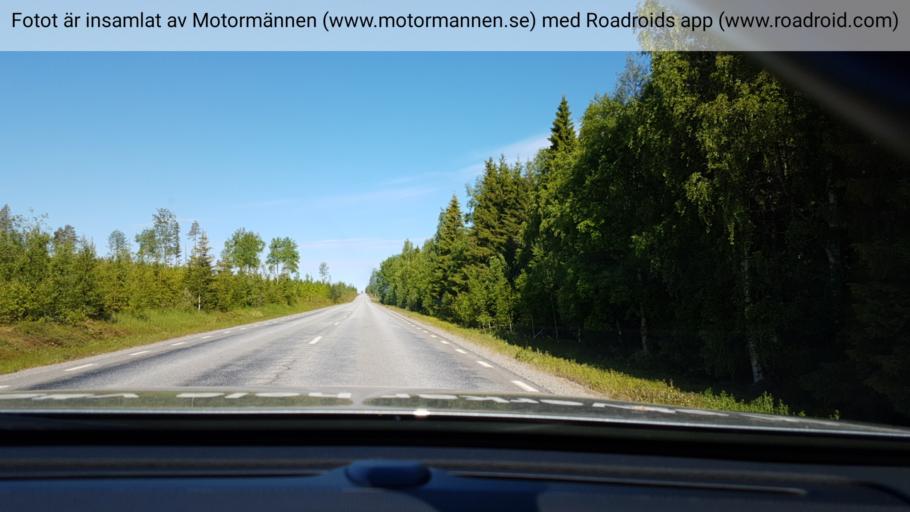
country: SE
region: Vaesterbotten
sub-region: Bjurholms Kommun
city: Bjurholm
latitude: 63.9477
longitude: 18.9049
